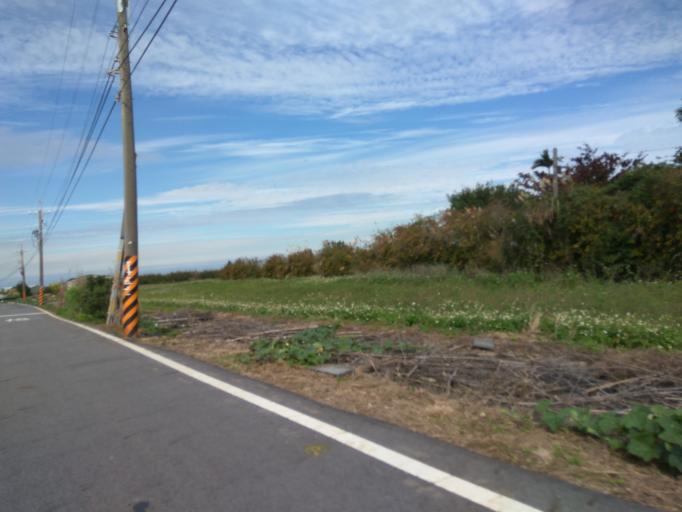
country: TW
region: Taiwan
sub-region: Hsinchu
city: Zhubei
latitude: 25.0031
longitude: 121.0848
